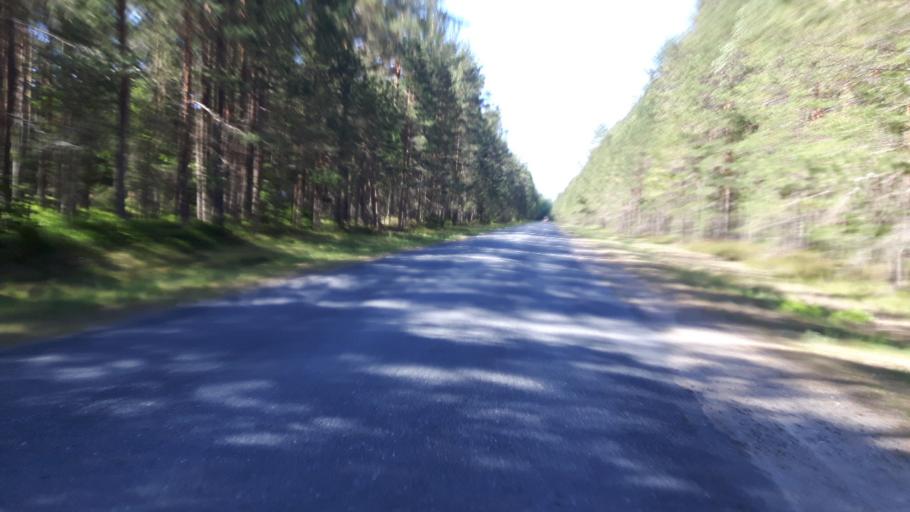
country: EE
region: Harju
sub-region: Loksa linn
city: Loksa
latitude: 59.5671
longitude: 25.6987
